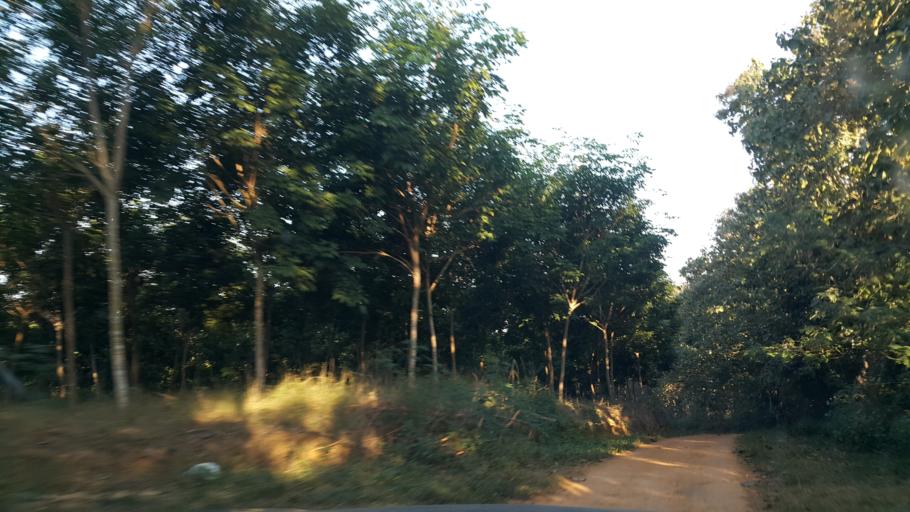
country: TH
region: Sukhothai
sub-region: Amphoe Si Satchanalai
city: Si Satchanalai
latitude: 17.5871
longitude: 99.6116
